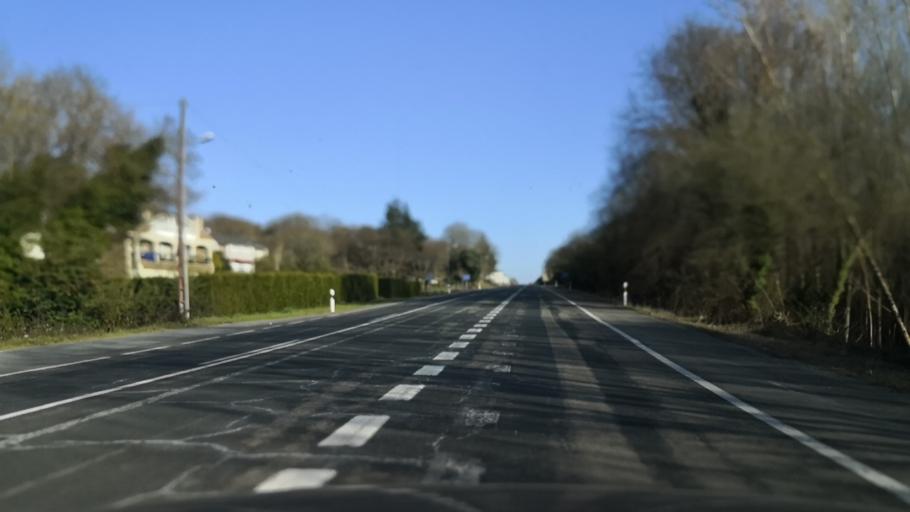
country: ES
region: Galicia
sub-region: Provincia de Lugo
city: Corgo
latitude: 42.9604
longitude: -7.4773
